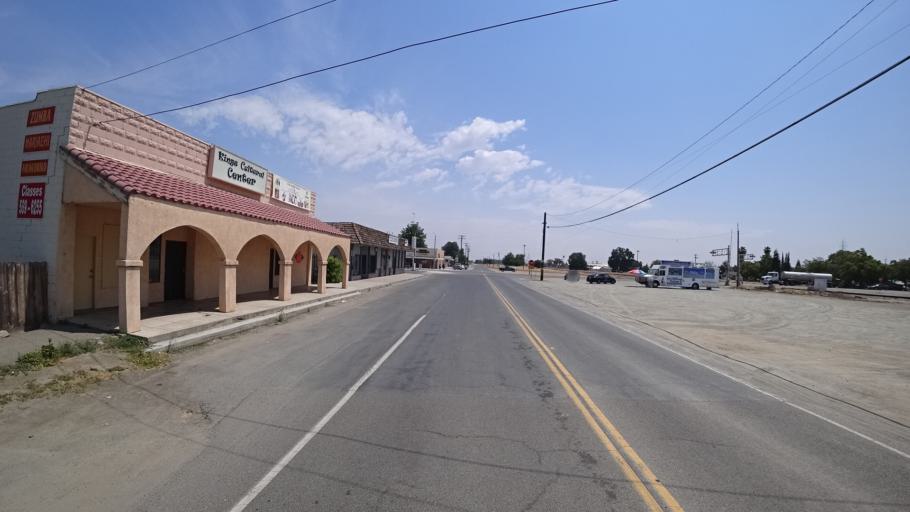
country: US
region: California
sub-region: Kings County
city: Armona
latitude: 36.3156
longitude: -119.7099
